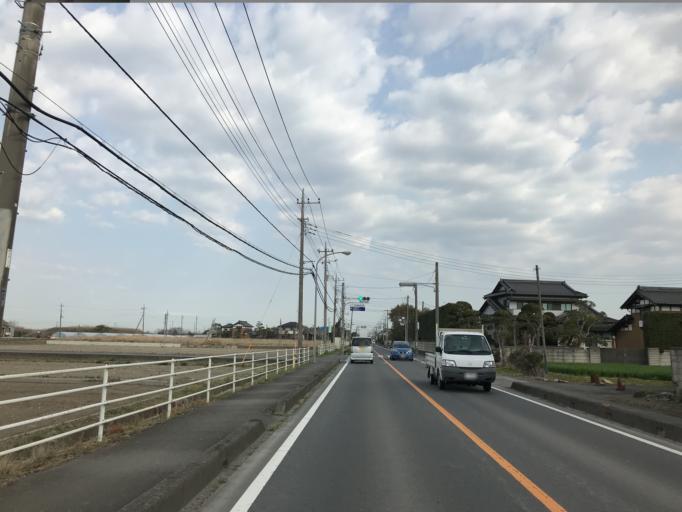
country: JP
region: Ibaraki
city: Mitsukaido
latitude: 35.9952
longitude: 140.0164
